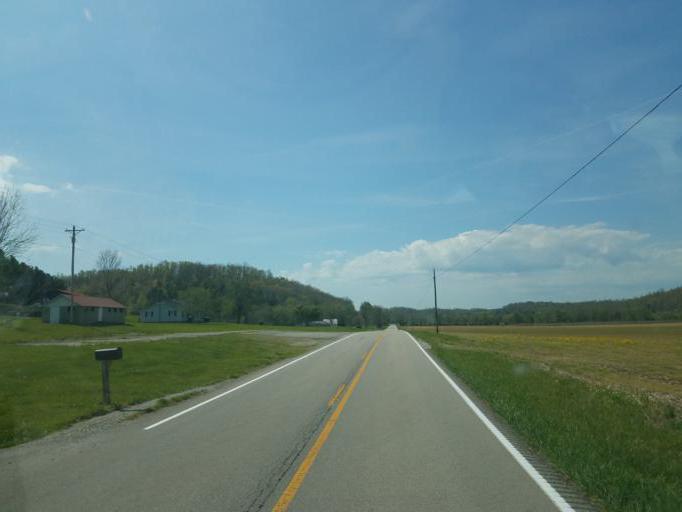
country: US
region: Kentucky
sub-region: Edmonson County
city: Brownsville
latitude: 37.2966
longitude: -86.4342
